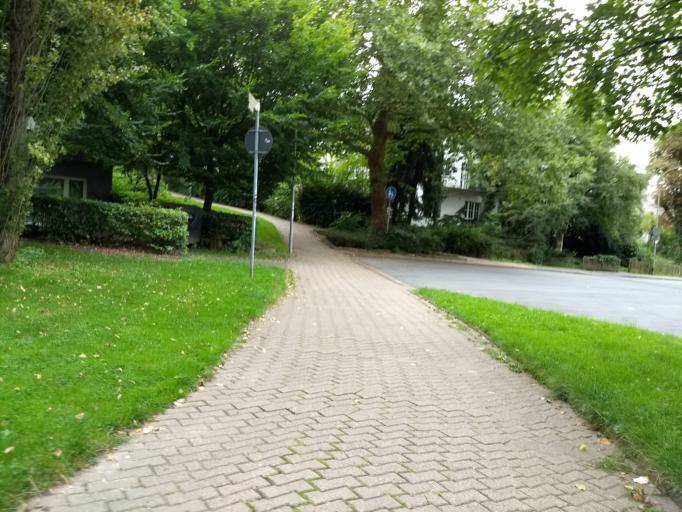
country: DE
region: North Rhine-Westphalia
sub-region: Regierungsbezirk Detmold
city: Paderborn
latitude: 51.7105
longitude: 8.7686
